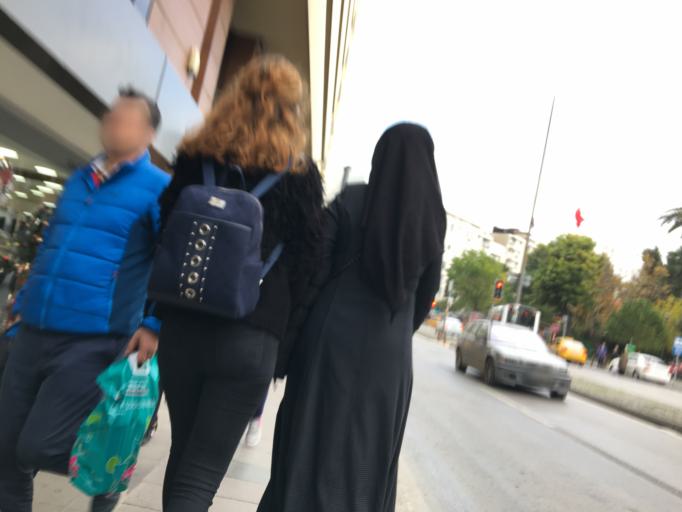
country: TR
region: Izmir
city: Izmir
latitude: 38.4343
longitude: 27.1414
